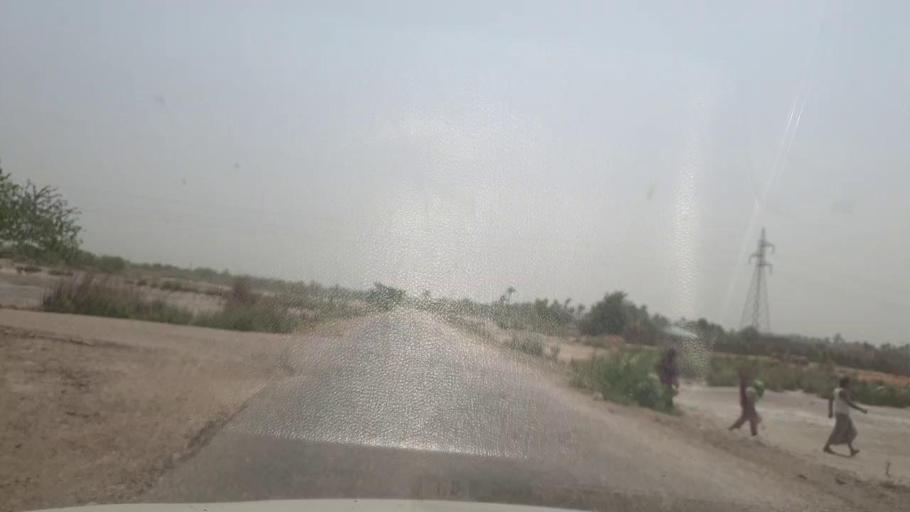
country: PK
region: Sindh
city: Kot Diji
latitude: 27.3760
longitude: 68.7016
